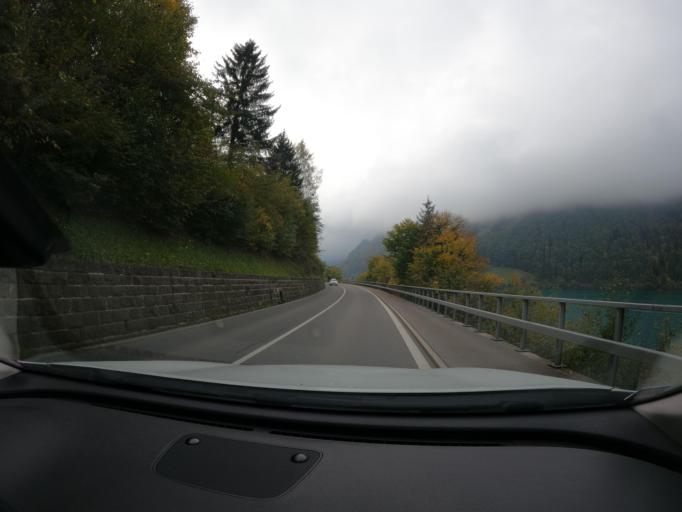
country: CH
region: Obwalden
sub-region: Obwalden
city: Lungern
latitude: 46.7990
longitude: 8.1640
